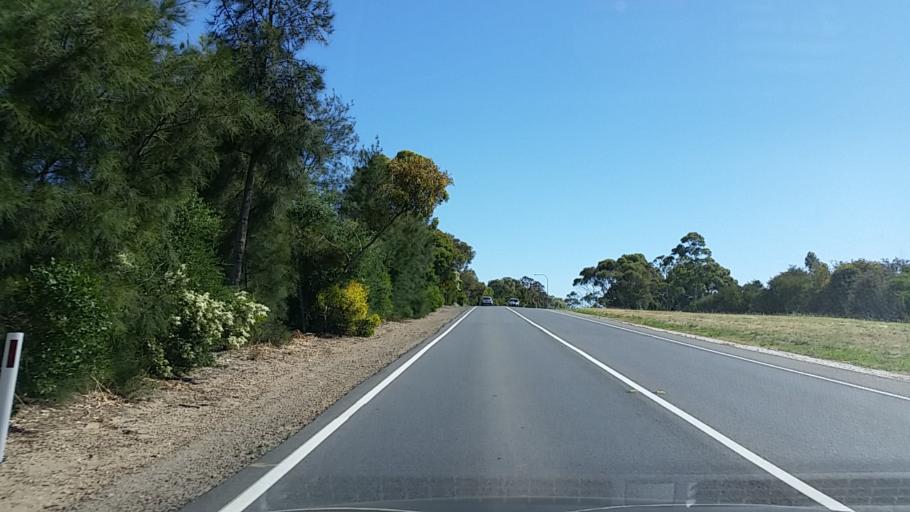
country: AU
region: South Australia
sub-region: Tea Tree Gully
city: Hope Valley
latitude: -34.8010
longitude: 138.7056
